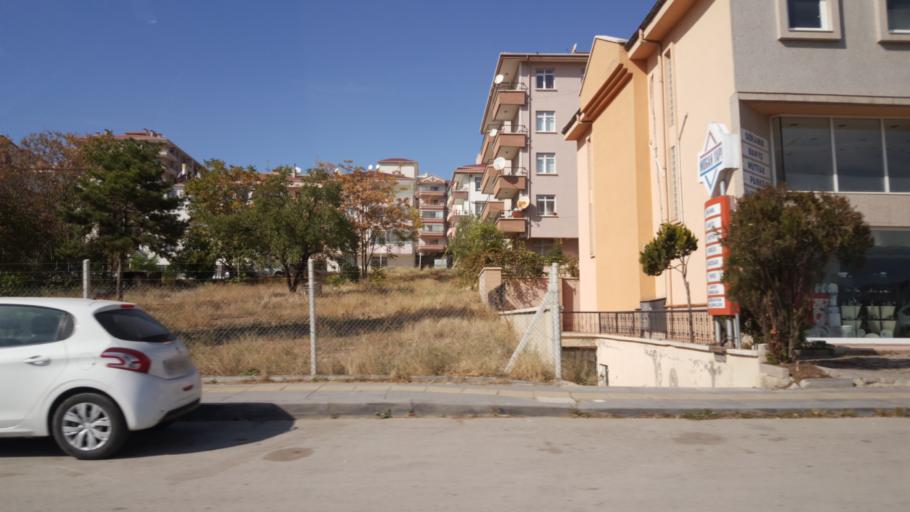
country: TR
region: Ankara
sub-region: Goelbasi
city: Golbasi
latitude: 39.8033
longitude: 32.8004
